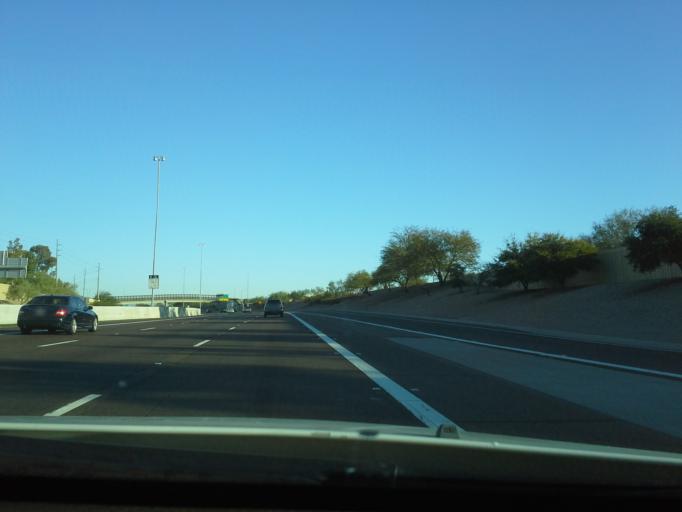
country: US
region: Arizona
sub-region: Maricopa County
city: Paradise Valley
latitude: 33.6299
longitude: -112.0050
